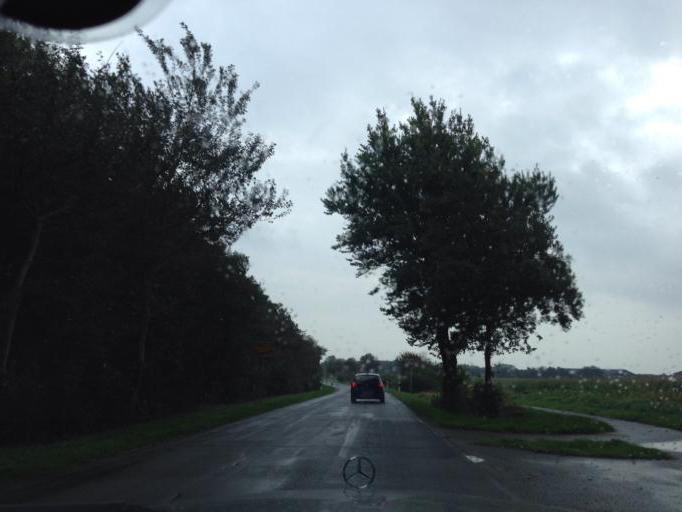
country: DE
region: Schleswig-Holstein
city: Borgsum
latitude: 54.6969
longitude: 8.4638
